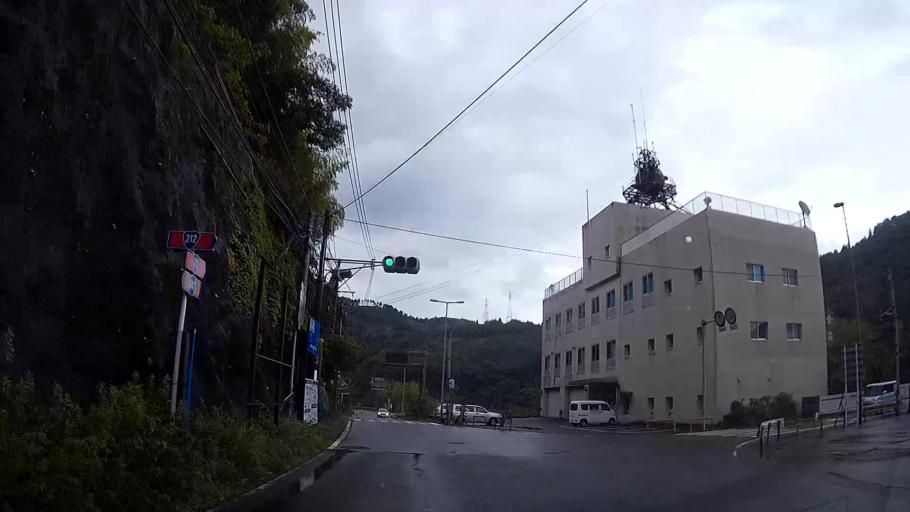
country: JP
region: Oita
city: Hita
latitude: 33.1945
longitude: 130.9923
